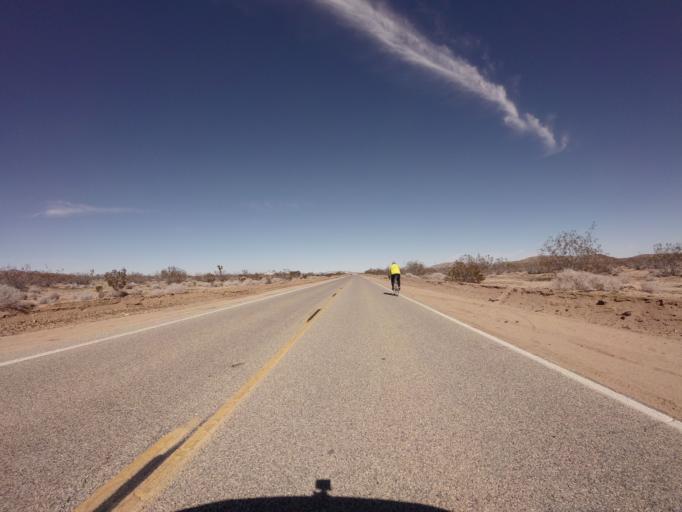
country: US
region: California
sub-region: San Bernardino County
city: Yucca Valley
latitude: 34.2399
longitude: -116.3933
